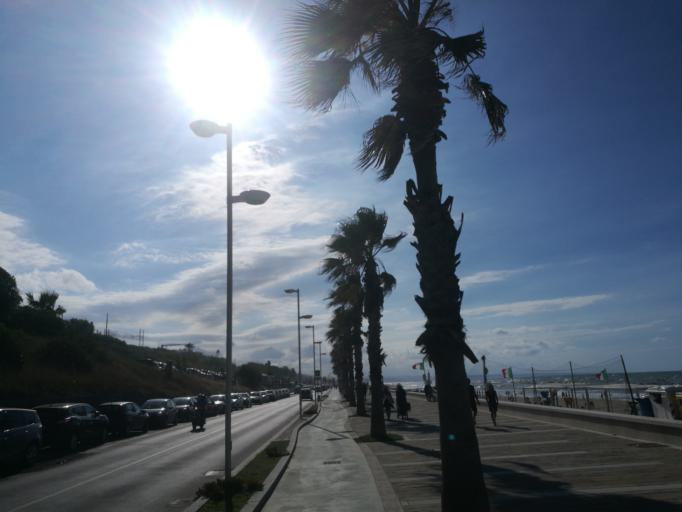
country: IT
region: Molise
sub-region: Provincia di Campobasso
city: Termoli
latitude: 42.0061
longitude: 14.9811
